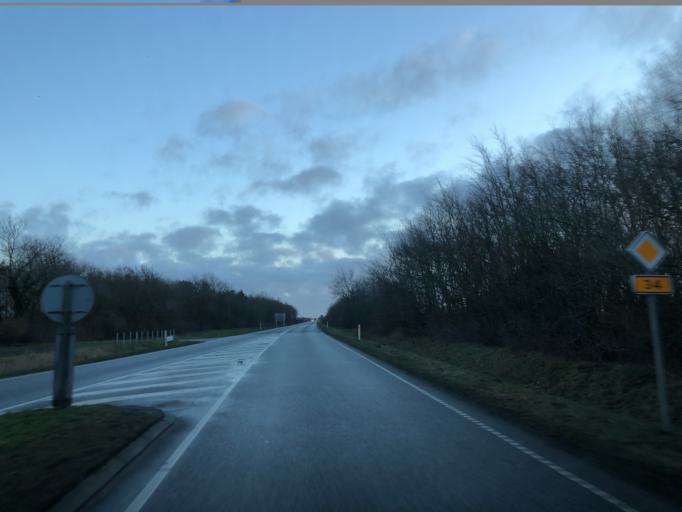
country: DK
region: Central Jutland
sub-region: Herning Kommune
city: Sunds
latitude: 56.2655
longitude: 9.0041
